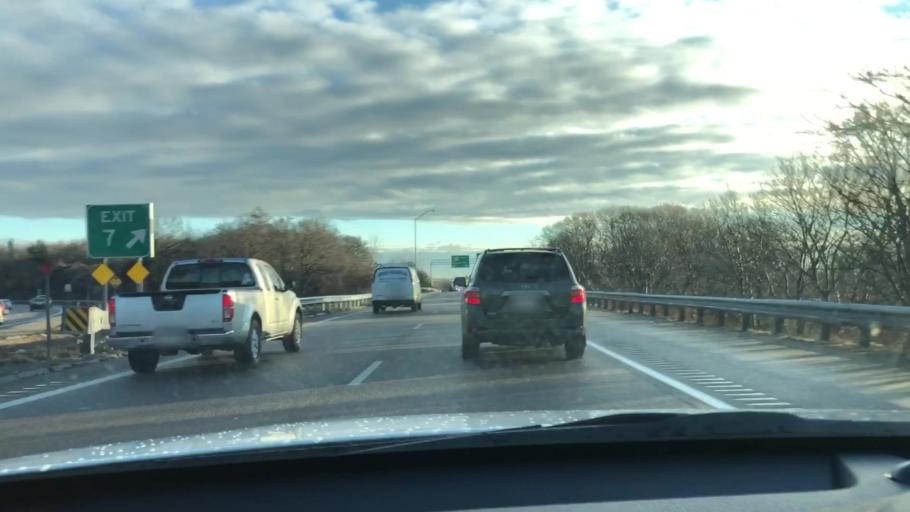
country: US
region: Massachusetts
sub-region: Norfolk County
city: Braintree
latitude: 42.2244
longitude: -71.0226
